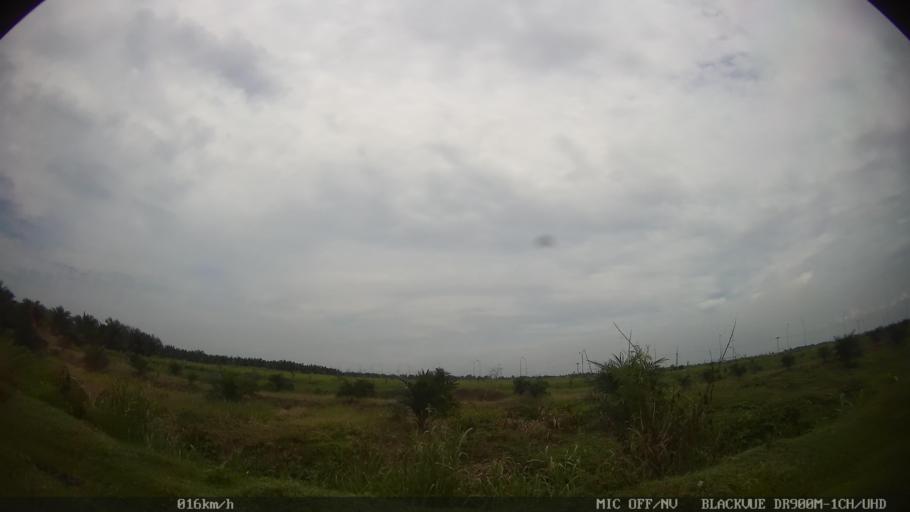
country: ID
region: North Sumatra
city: Sunggal
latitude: 3.6273
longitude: 98.5807
